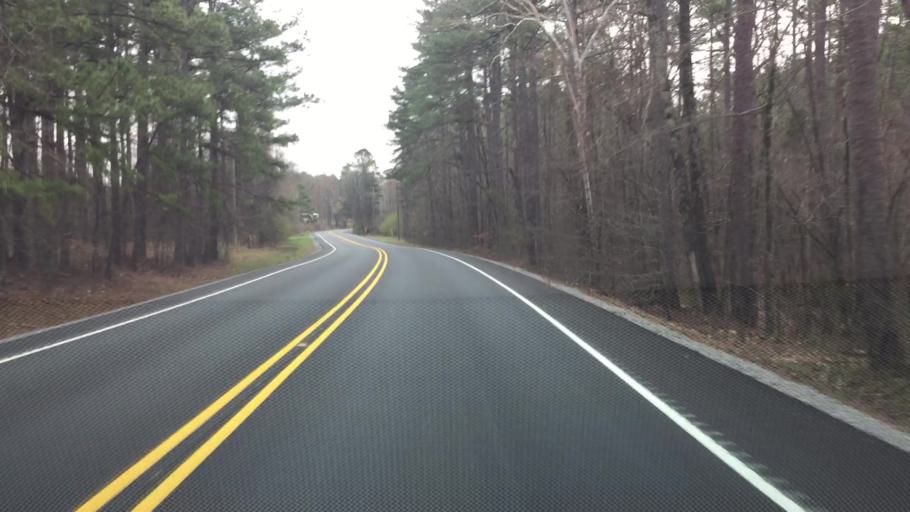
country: US
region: Arkansas
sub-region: Saline County
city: Haskell
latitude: 34.6133
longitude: -92.7930
